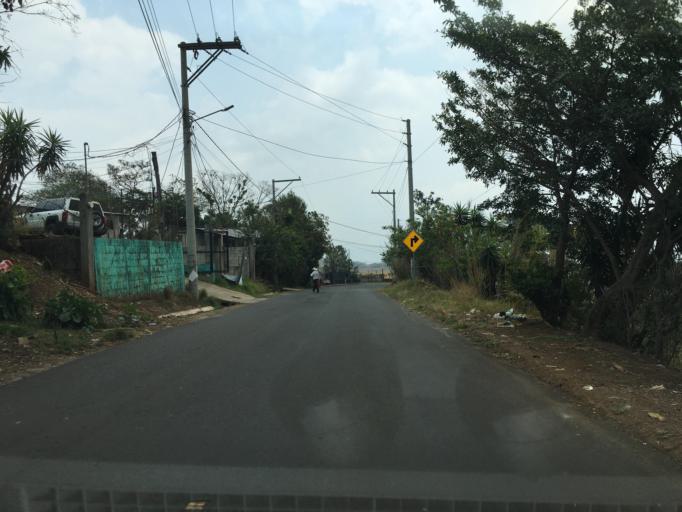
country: GT
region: Escuintla
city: San Vicente Pacaya
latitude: 14.3361
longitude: -90.5666
